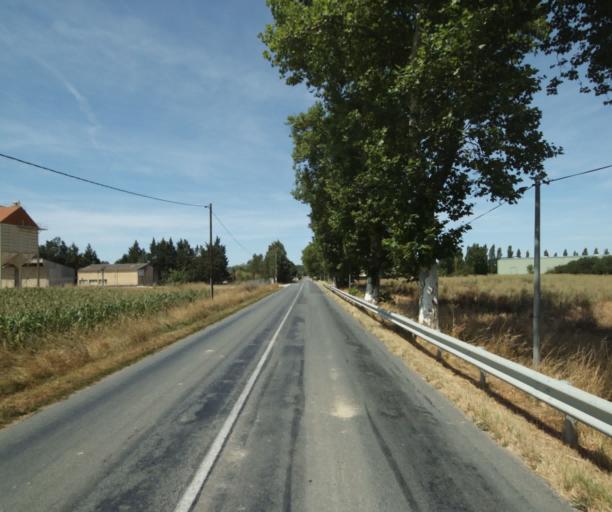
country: FR
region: Midi-Pyrenees
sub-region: Departement de la Haute-Garonne
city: Revel
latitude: 43.5141
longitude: 2.0102
